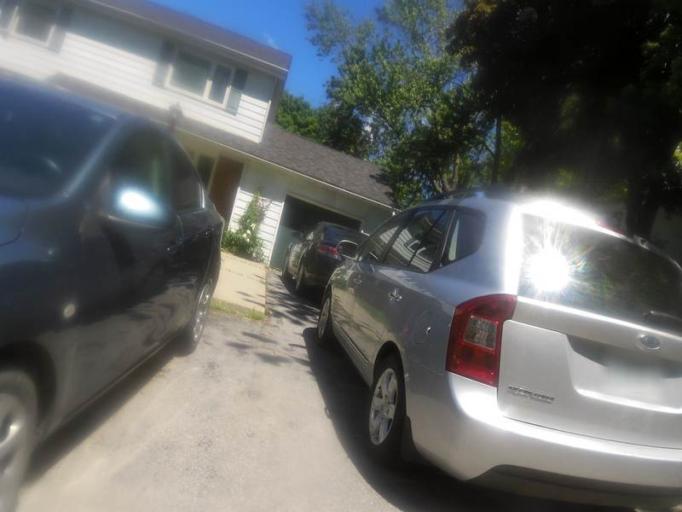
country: CA
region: Ontario
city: Kingston
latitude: 44.2398
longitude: -76.5323
